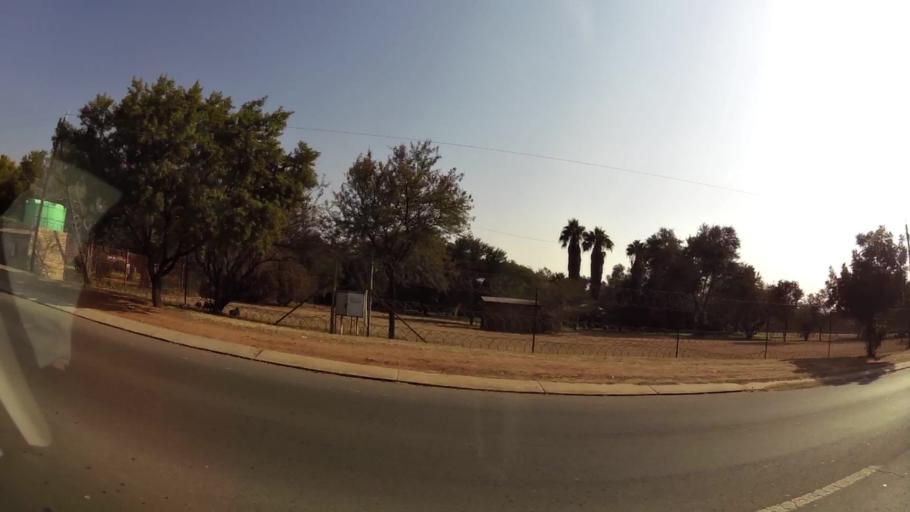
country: ZA
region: Gauteng
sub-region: City of Tshwane Metropolitan Municipality
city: Pretoria
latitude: -25.7633
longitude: 28.3330
